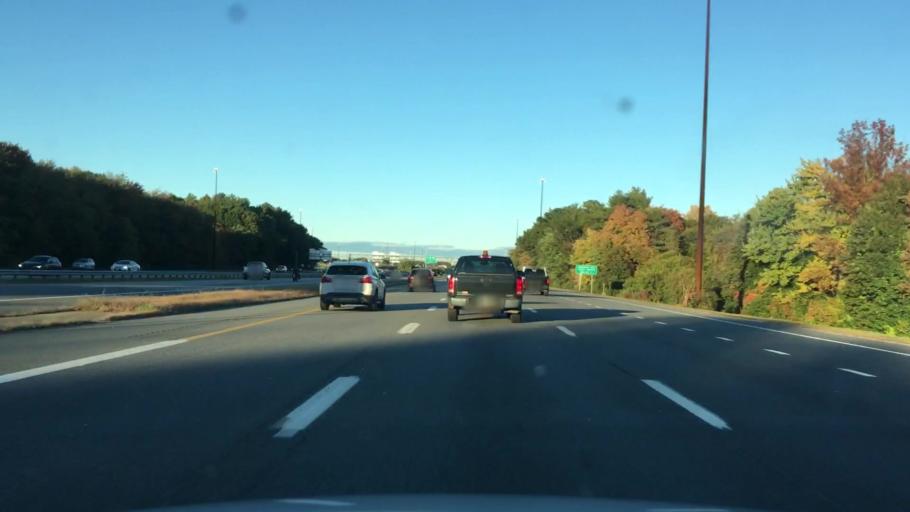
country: US
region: New Hampshire
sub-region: Rockingham County
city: Portsmouth
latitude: 43.0631
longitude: -70.7959
